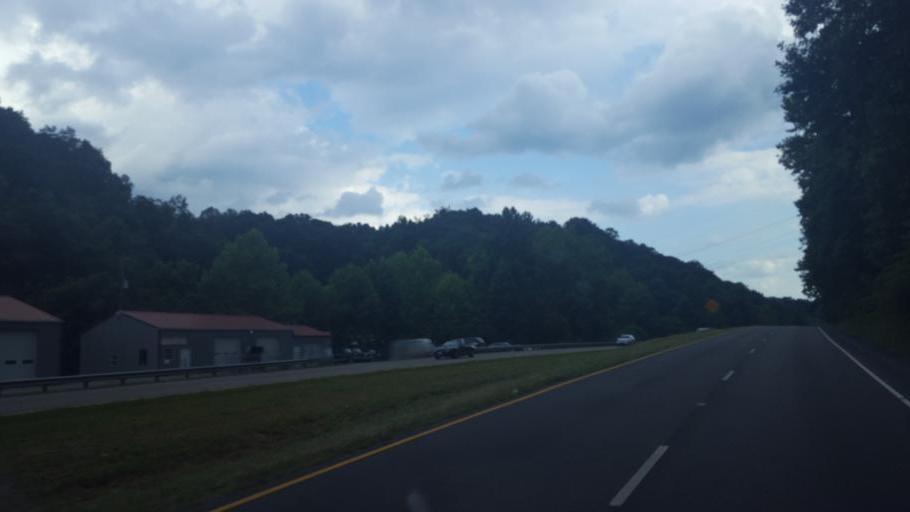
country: US
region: Virginia
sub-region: Wise County
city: Pound
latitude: 37.0829
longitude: -82.5986
